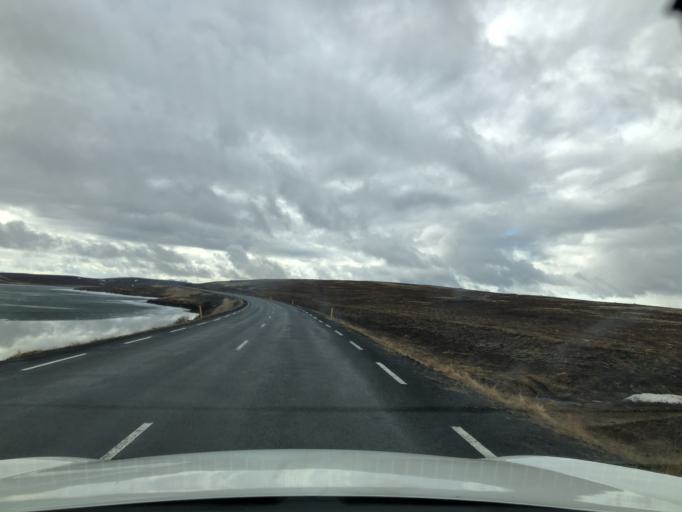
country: IS
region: Northeast
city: Laugar
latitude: 65.6418
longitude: -17.2614
